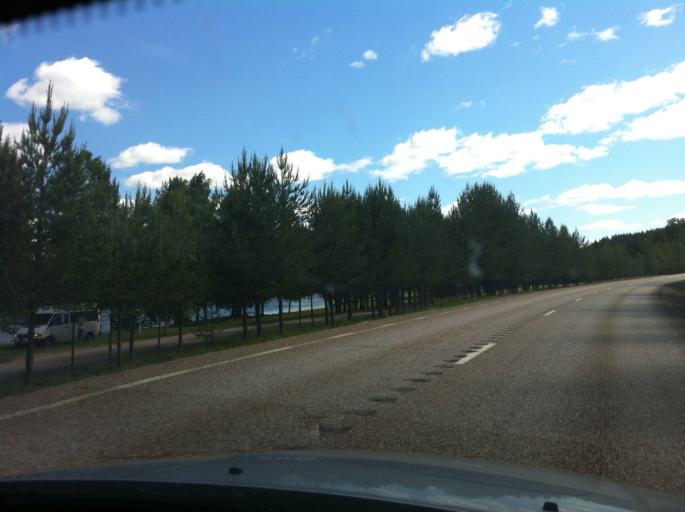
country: SE
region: Gaevleborg
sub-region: Ljusdals Kommun
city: Farila
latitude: 61.9624
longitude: 15.3570
